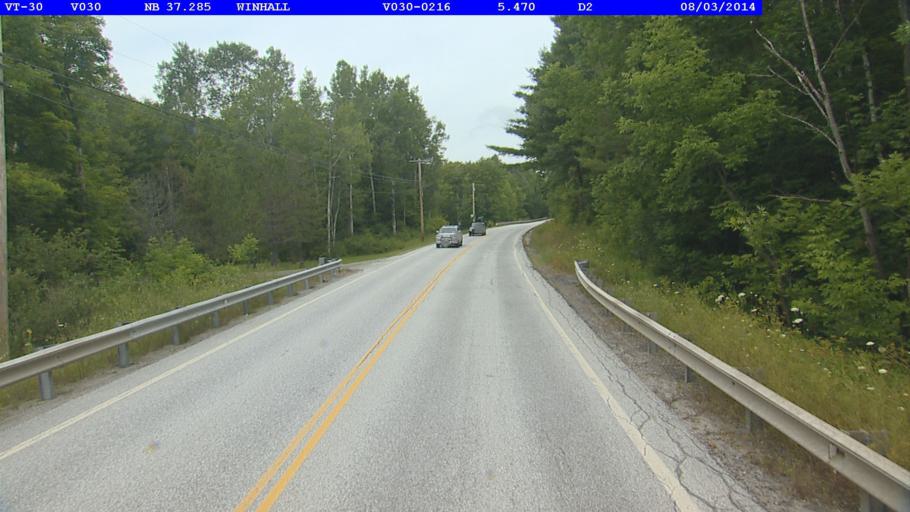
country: US
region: Vermont
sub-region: Bennington County
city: Manchester Center
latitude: 43.1856
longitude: -72.9352
